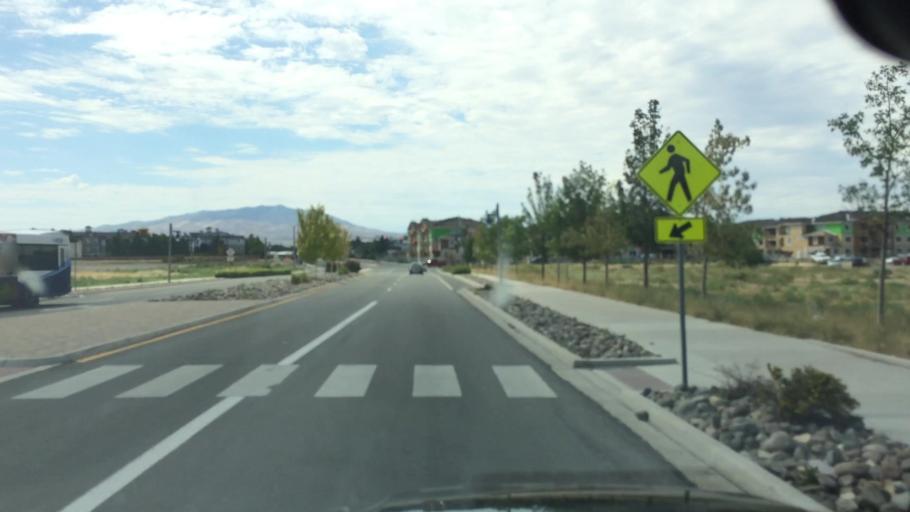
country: US
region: Nevada
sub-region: Washoe County
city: Sparks
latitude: 39.5361
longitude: -119.7205
